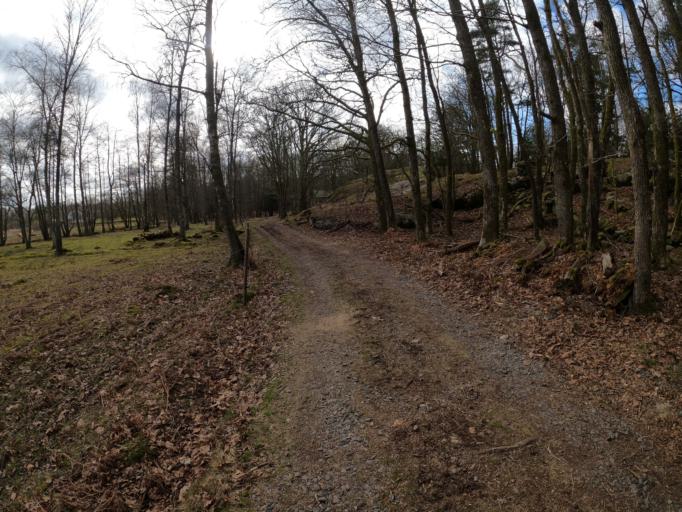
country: SE
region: Vaestra Goetaland
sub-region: Harryda Kommun
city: Molnlycke
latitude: 57.6315
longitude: 12.0881
